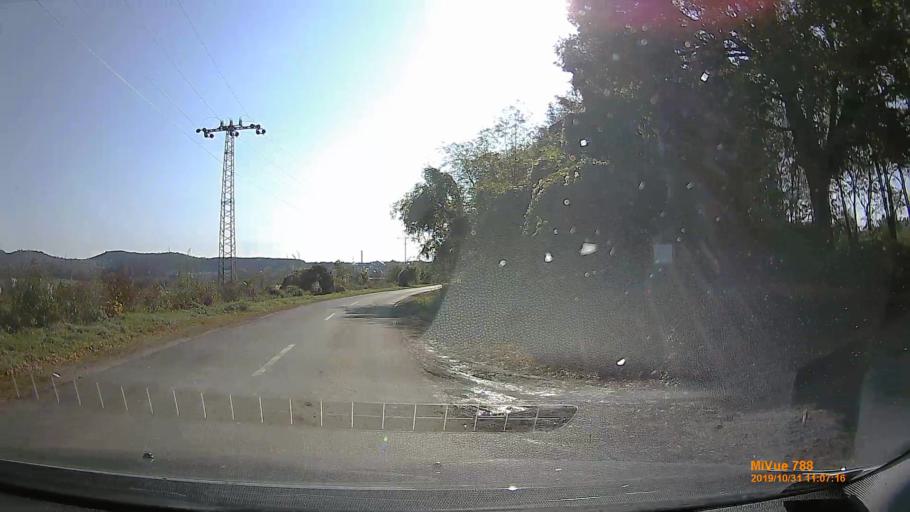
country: HU
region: Pest
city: Pilisborosjeno
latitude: 47.5980
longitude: 18.9983
